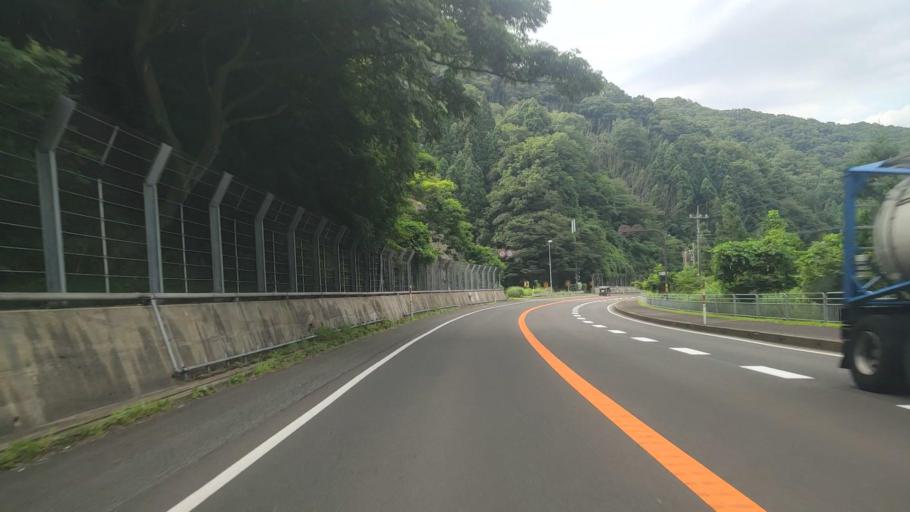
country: JP
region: Fukui
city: Takefu
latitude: 35.8080
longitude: 136.0950
